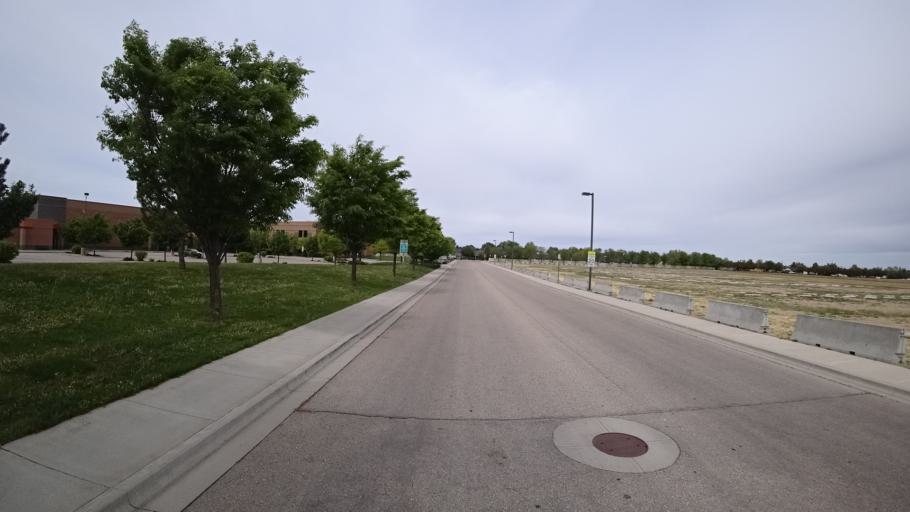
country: US
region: Idaho
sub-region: Ada County
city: Garden City
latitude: 43.5718
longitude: -116.2844
